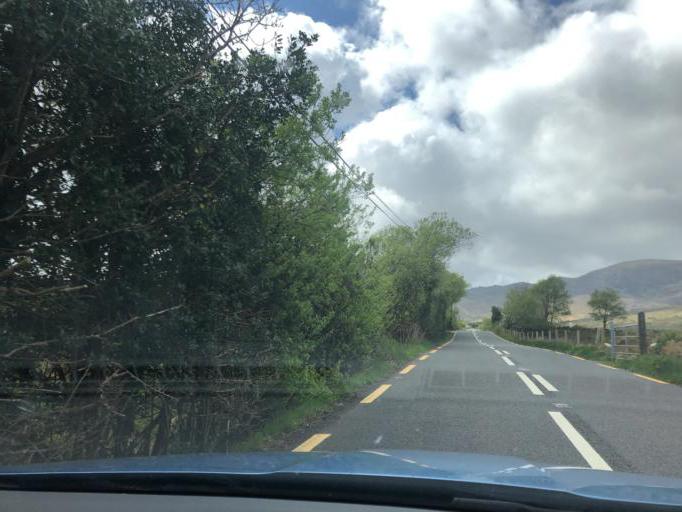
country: IE
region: Munster
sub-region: Ciarrai
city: Cahersiveen
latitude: 51.8298
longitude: -9.9409
